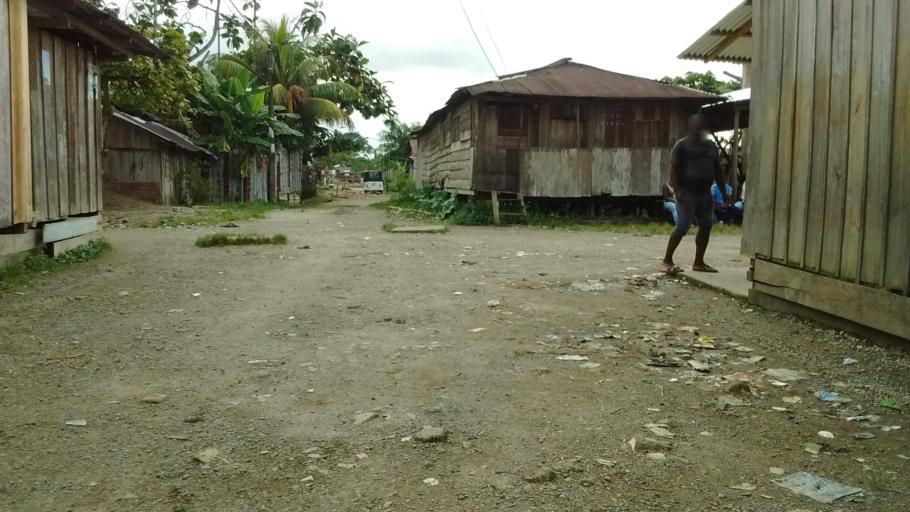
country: CO
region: Cauca
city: Guapi
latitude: 2.5697
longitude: -77.8865
